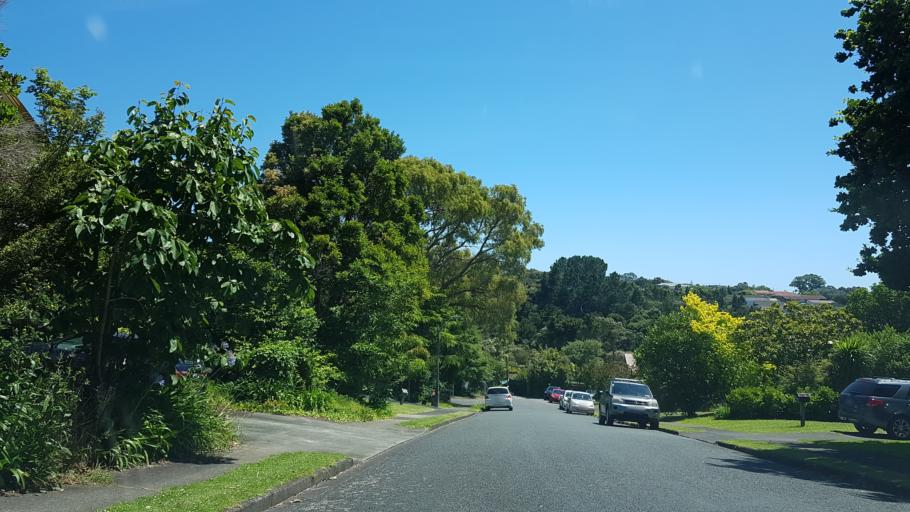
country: NZ
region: Auckland
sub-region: Auckland
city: North Shore
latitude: -36.8073
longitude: 174.7379
